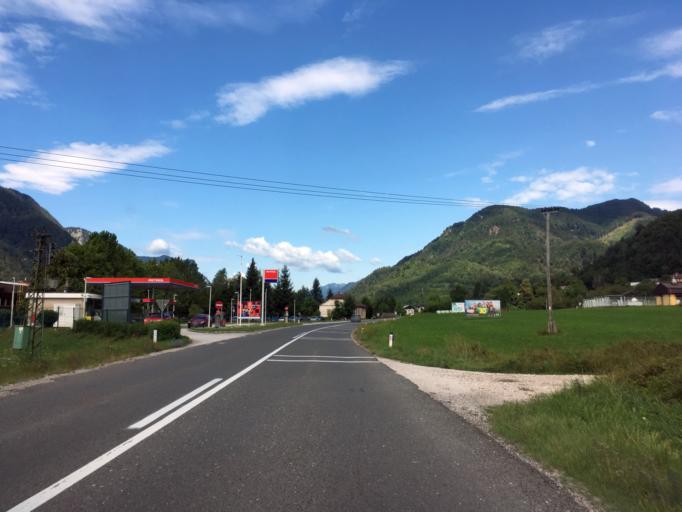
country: SI
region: Jesenice
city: Slovenski Javornik
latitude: 46.4226
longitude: 14.1036
